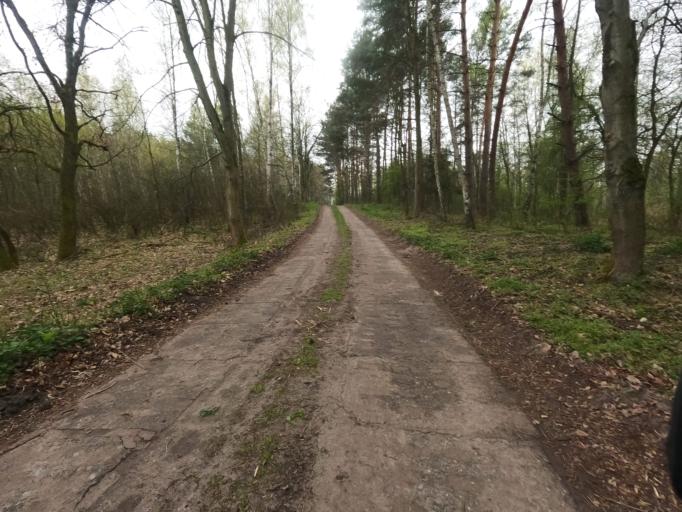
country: PL
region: West Pomeranian Voivodeship
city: Trzcinsko Zdroj
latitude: 52.9156
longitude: 14.5573
